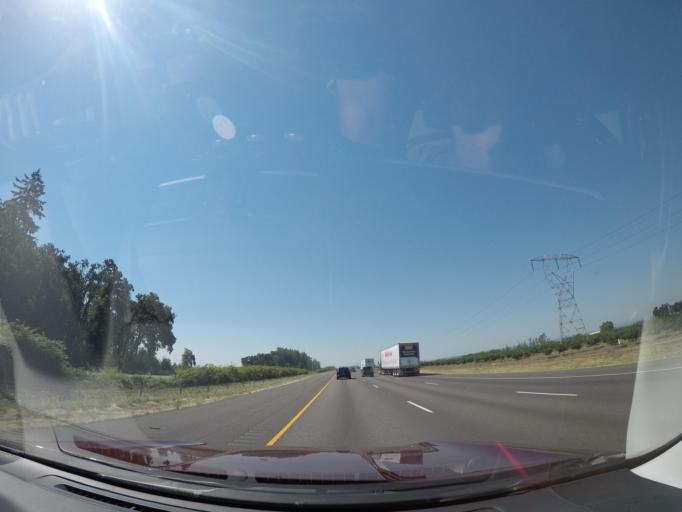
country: US
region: Oregon
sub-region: Marion County
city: Gervais
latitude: 45.0701
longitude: -122.9618
